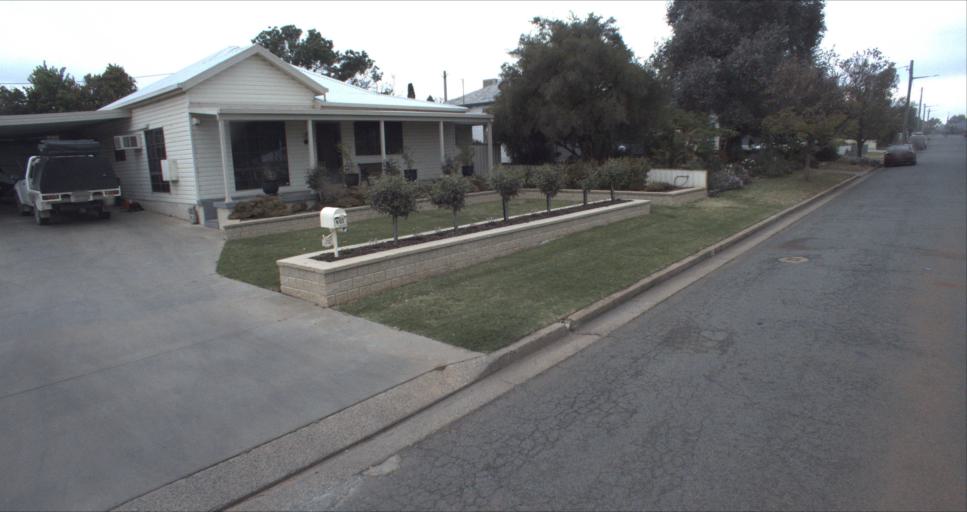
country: AU
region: New South Wales
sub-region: Leeton
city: Leeton
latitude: -34.5491
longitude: 146.4019
